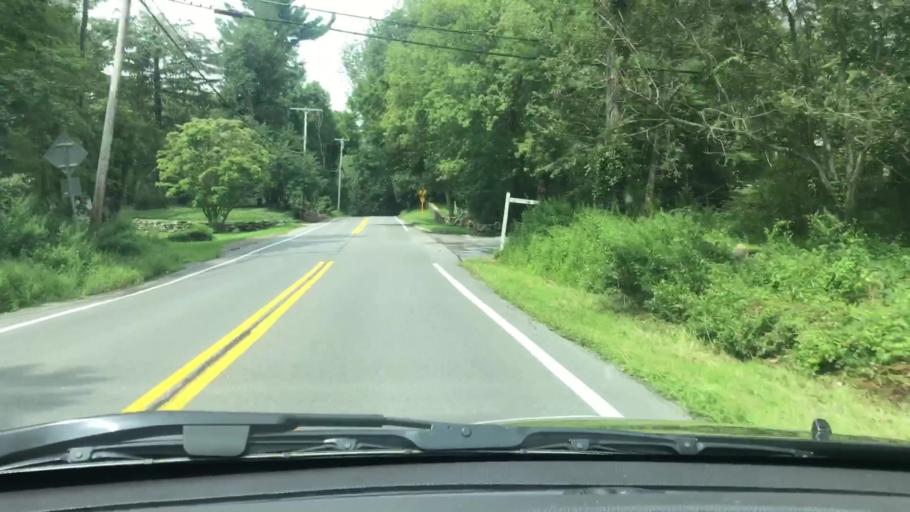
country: US
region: New York
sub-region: Westchester County
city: Pound Ridge
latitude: 41.1729
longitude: -73.6039
